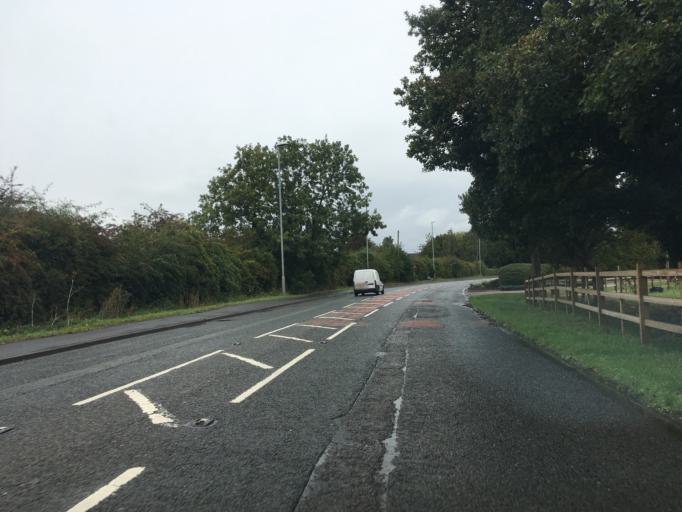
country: GB
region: England
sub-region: Nottinghamshire
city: Ruddington
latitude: 52.8630
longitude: -1.1337
